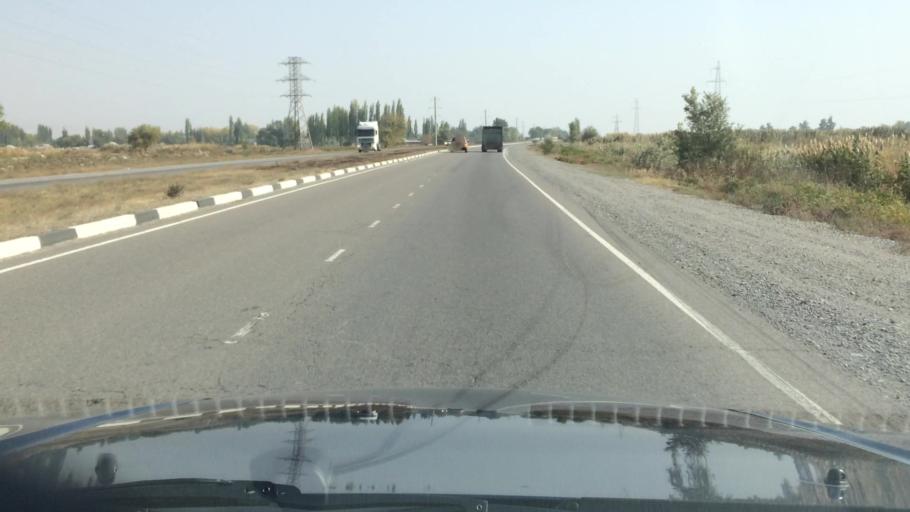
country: KG
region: Chuy
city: Kant
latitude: 42.9673
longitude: 74.8258
